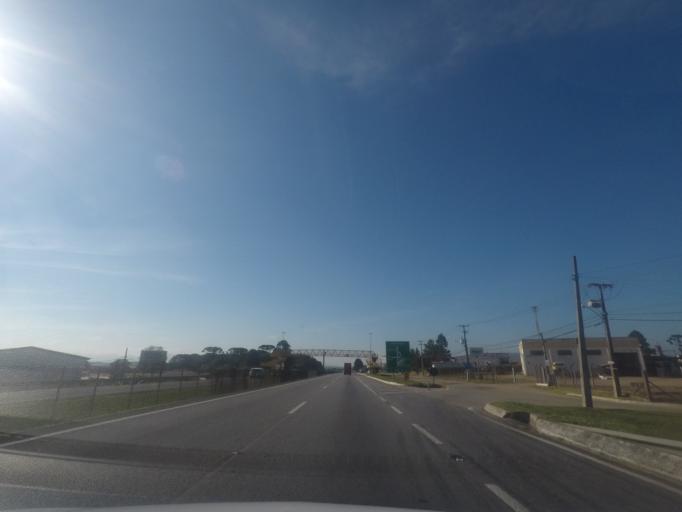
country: BR
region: Parana
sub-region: Sao Jose Dos Pinhais
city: Sao Jose dos Pinhais
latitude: -25.5079
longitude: -49.1364
